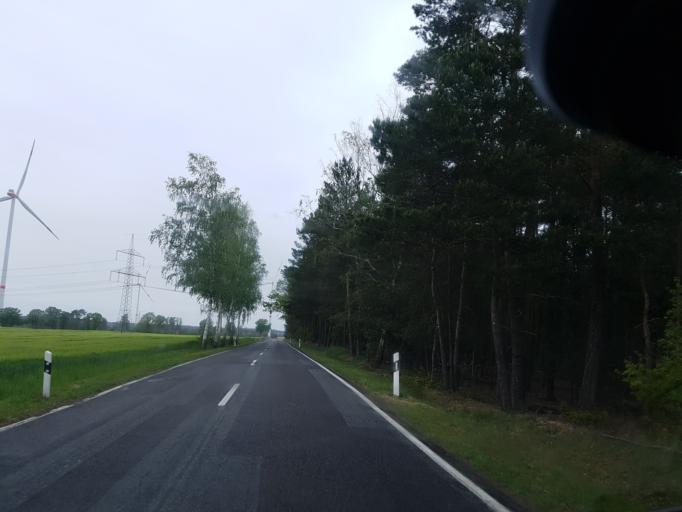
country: DE
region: Brandenburg
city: Drebkau
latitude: 51.6471
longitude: 14.2786
